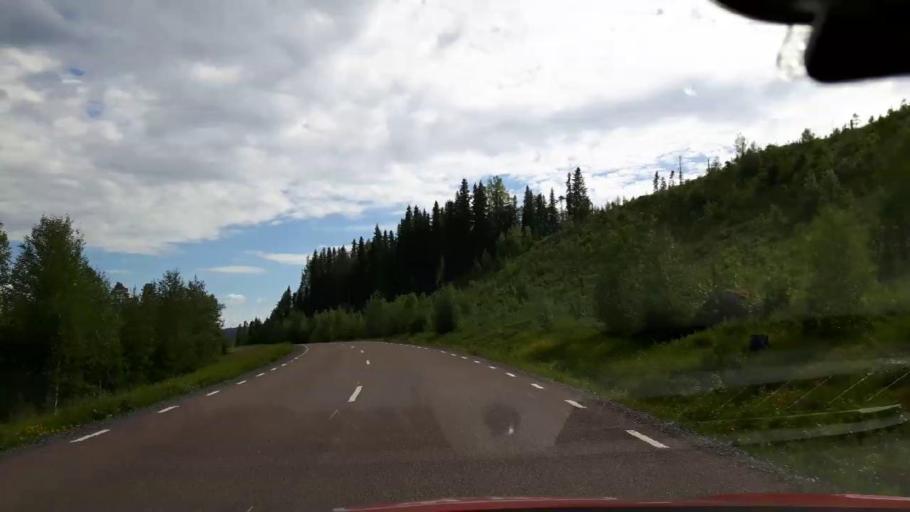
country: SE
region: Jaemtland
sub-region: Krokoms Kommun
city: Valla
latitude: 63.9388
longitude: 14.2212
